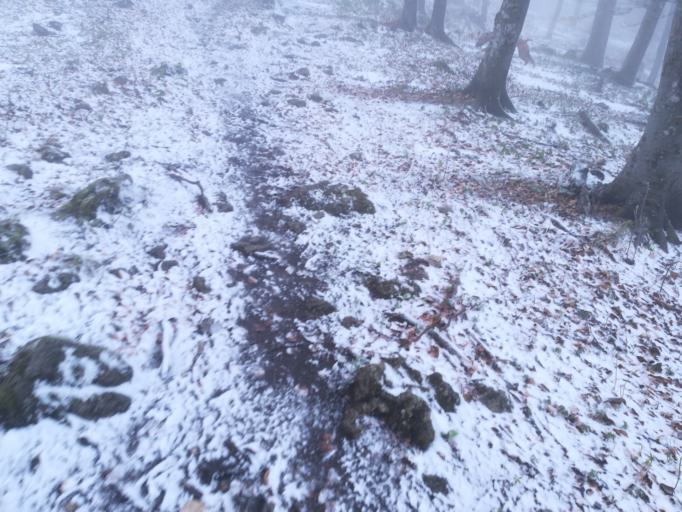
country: HR
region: Varazdinska
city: Ivanec
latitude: 46.1839
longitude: 16.1402
